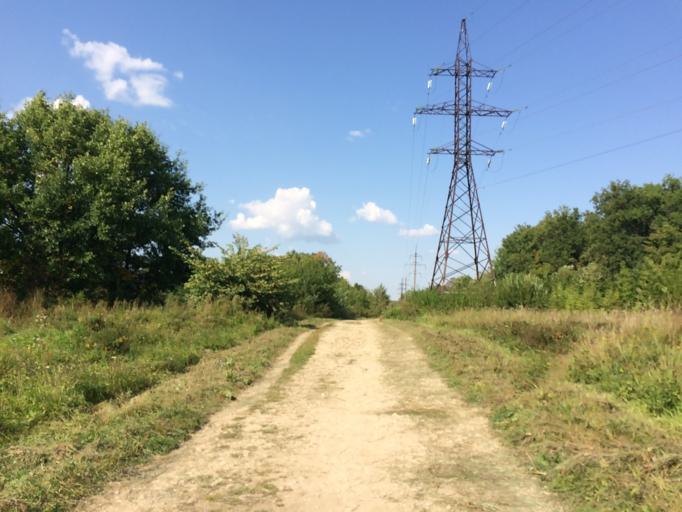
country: RU
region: Mariy-El
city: Yoshkar-Ola
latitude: 56.6142
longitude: 47.9316
